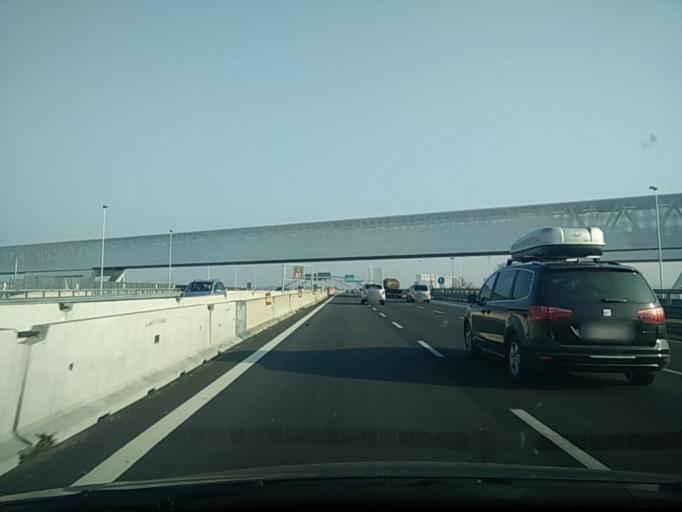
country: IT
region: Lombardy
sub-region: Citta metropolitana di Milano
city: Pero
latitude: 45.5148
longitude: 9.1020
